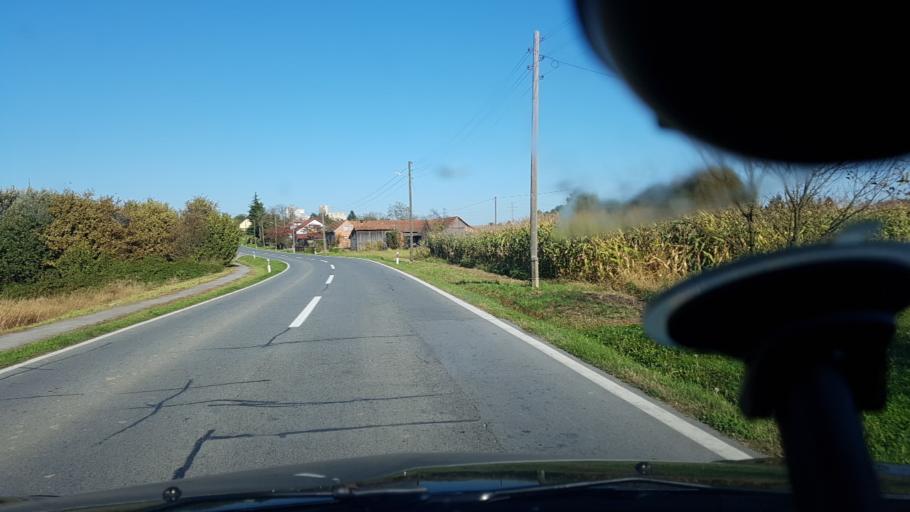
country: HR
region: Bjelovarsko-Bilogorska
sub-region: Grad Cazma
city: Cazma
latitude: 45.7808
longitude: 16.6422
